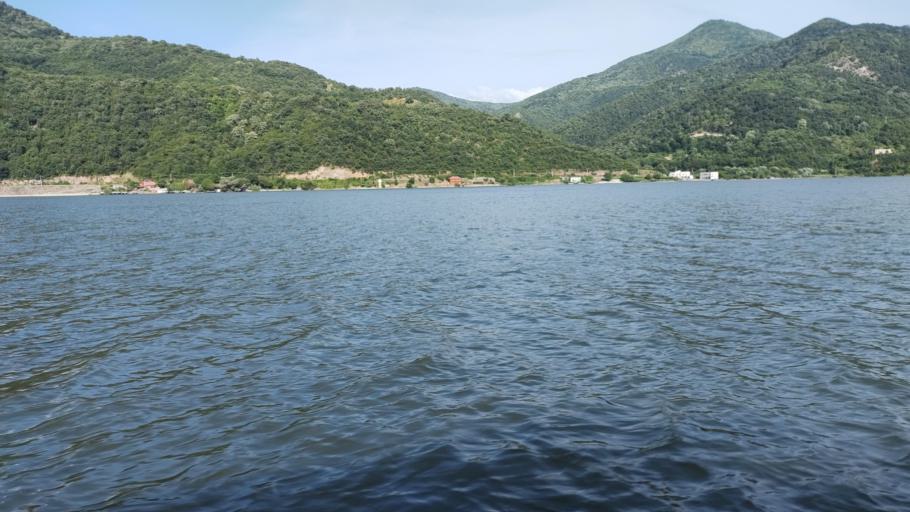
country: RO
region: Caras-Severin
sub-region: Comuna Berzasca
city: Berzasca
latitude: 44.5858
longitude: 22.0250
